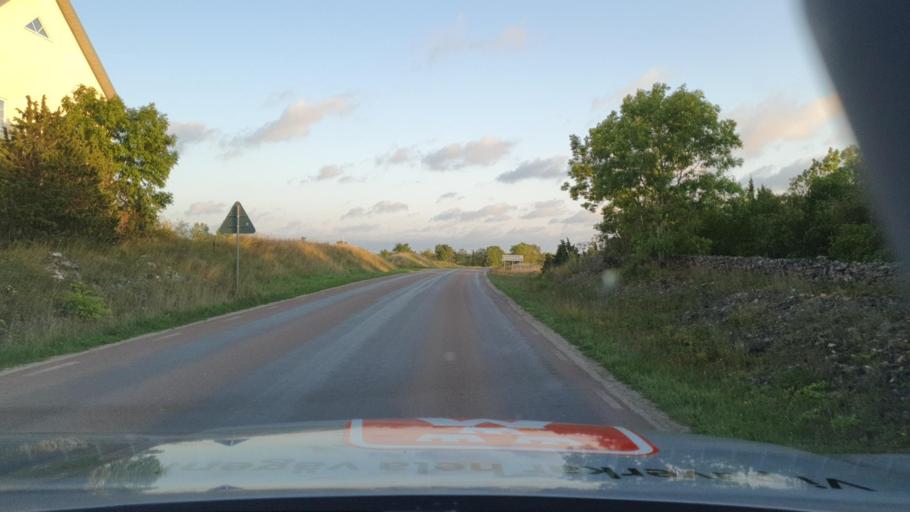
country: SE
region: Gotland
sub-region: Gotland
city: Visby
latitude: 57.6482
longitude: 18.5512
